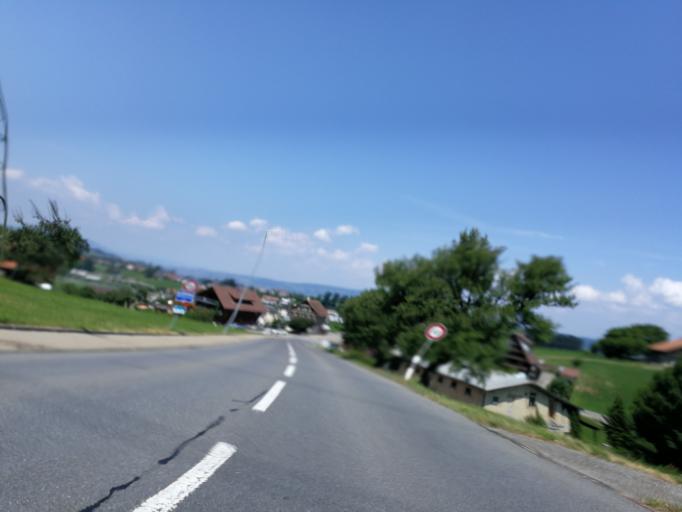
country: CH
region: Schwyz
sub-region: Bezirk Hoefe
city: Schindellegi
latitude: 47.1831
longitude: 8.7104
